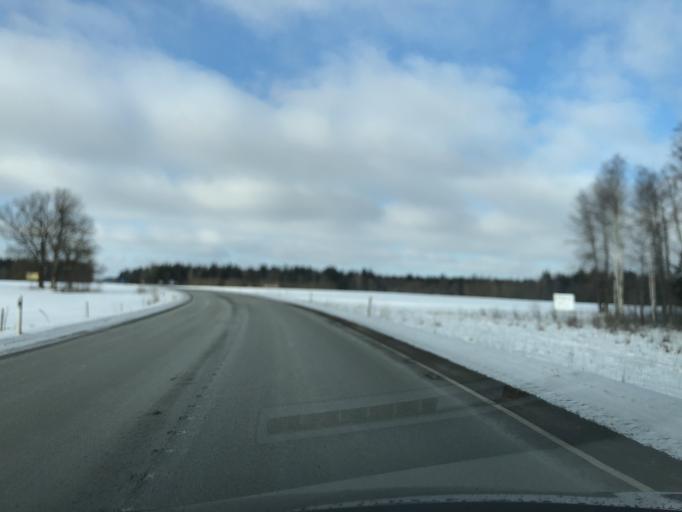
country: EE
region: Jaervamaa
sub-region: Paide linn
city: Paide
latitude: 58.8930
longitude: 25.6689
